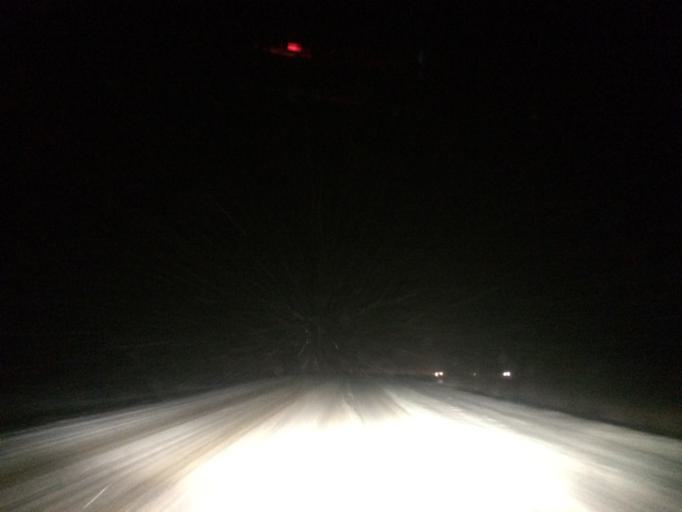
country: RU
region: Tula
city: Dubna
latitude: 54.0858
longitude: 37.0593
